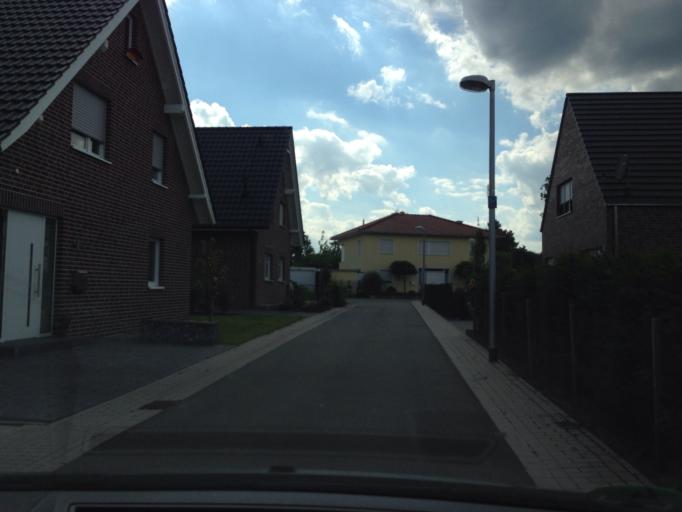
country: DE
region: North Rhine-Westphalia
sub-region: Regierungsbezirk Munster
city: Muenster
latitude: 51.9941
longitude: 7.5415
